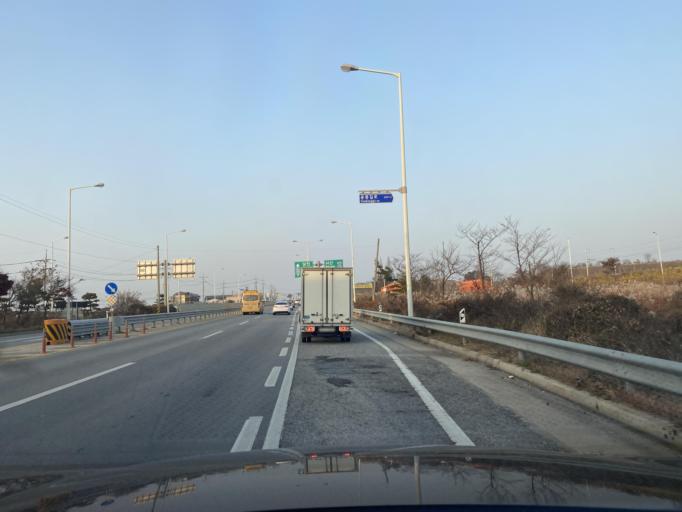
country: KR
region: Chungcheongnam-do
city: Yesan
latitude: 36.7042
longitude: 126.8304
